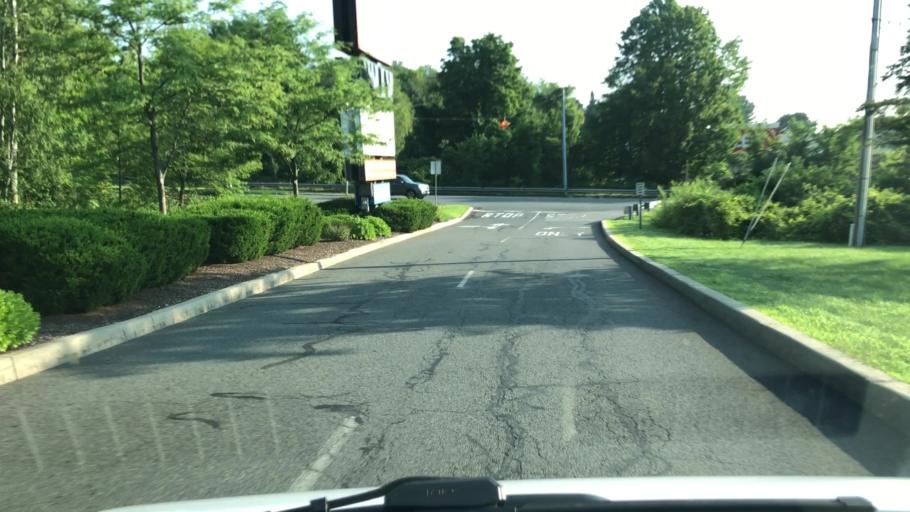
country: US
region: Massachusetts
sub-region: Franklin County
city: Greenfield
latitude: 42.5862
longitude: -72.6282
